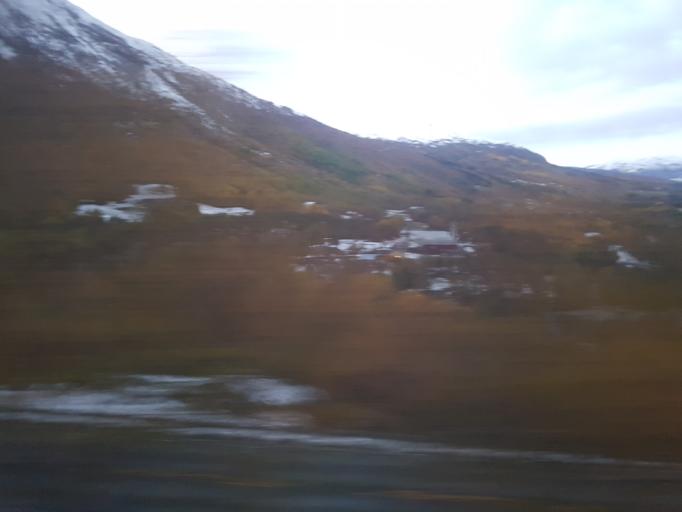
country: NO
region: Sor-Trondelag
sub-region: Oppdal
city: Oppdal
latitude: 62.5351
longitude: 9.6219
